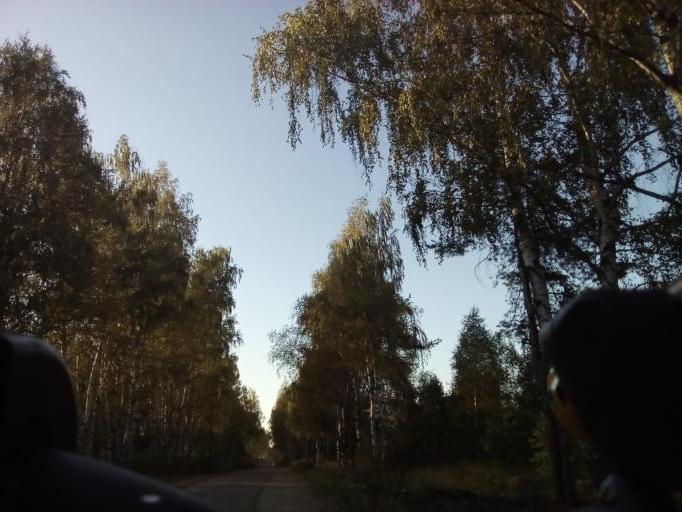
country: RU
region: Moskovskaya
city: Gzhel'
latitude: 55.6017
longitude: 38.3137
